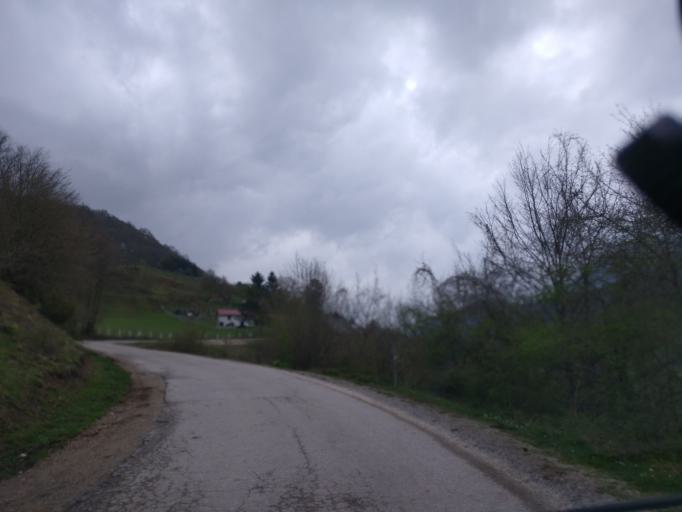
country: BA
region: Republika Srpska
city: Foca
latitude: 43.4388
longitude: 18.7630
